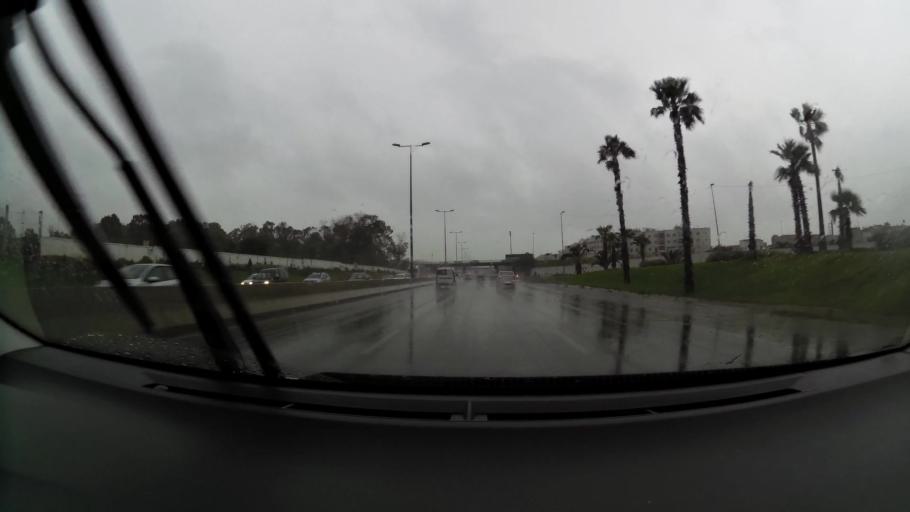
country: MA
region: Grand Casablanca
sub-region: Casablanca
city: Casablanca
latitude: 33.5668
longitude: -7.5767
